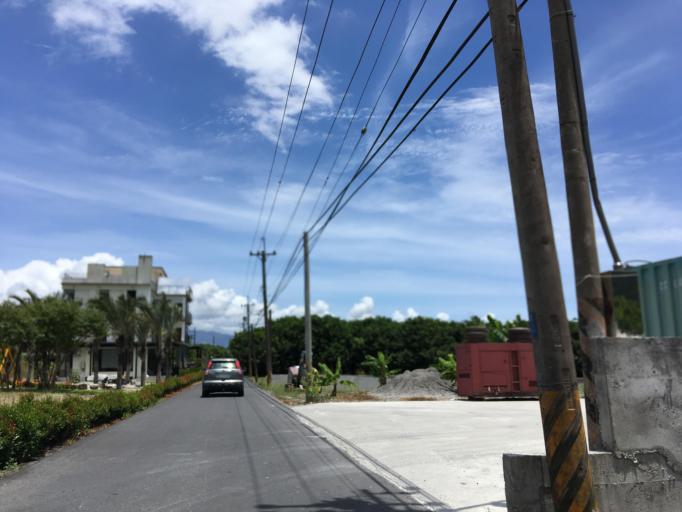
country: TW
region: Taiwan
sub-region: Yilan
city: Yilan
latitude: 24.6372
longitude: 121.7205
